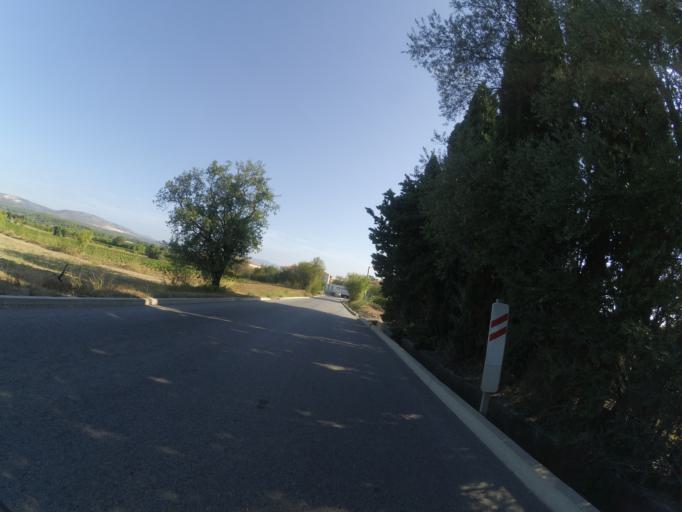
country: FR
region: Languedoc-Roussillon
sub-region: Departement des Pyrenees-Orientales
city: Peyrestortes
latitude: 42.7722
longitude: 2.8309
